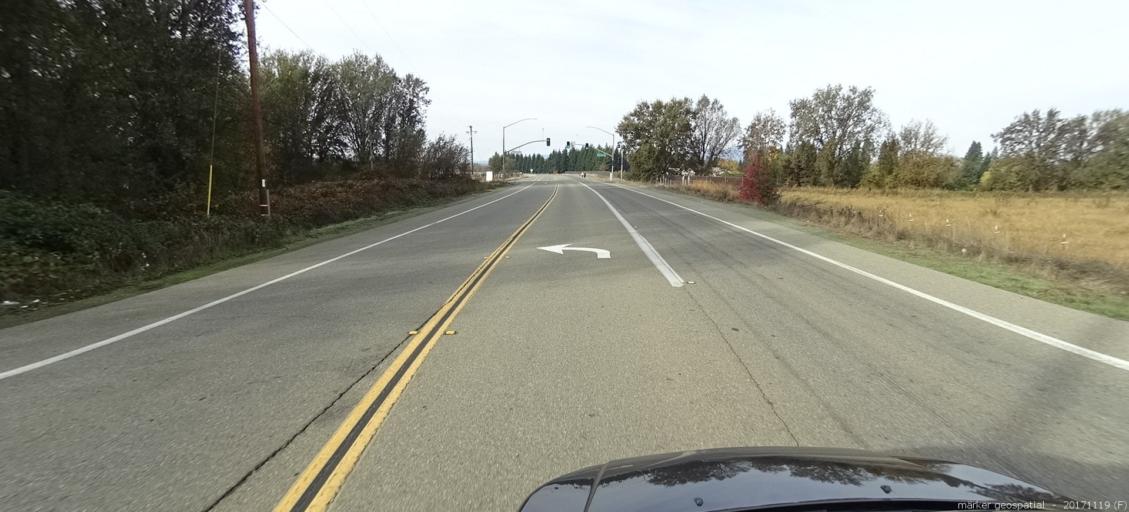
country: US
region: California
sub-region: Shasta County
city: Anderson
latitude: 40.5083
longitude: -122.3230
